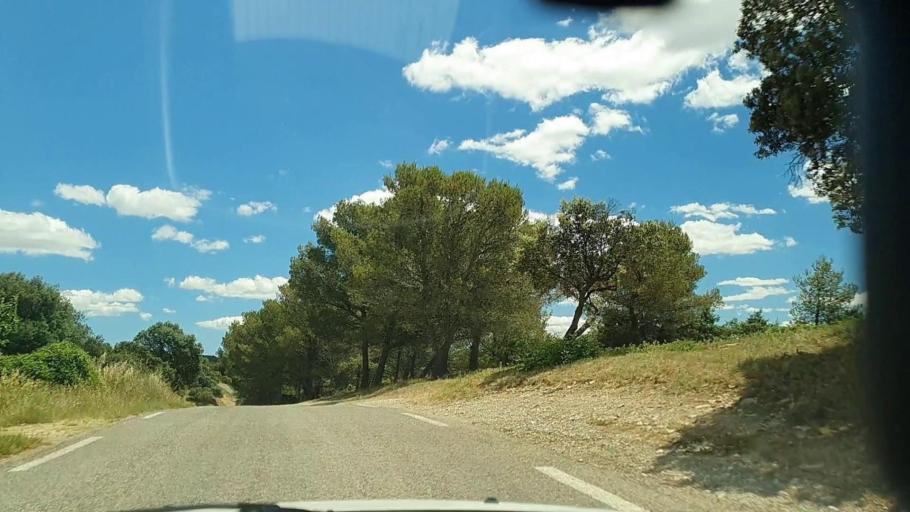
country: FR
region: Languedoc-Roussillon
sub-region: Departement du Gard
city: Cabrieres
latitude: 43.9101
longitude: 4.4494
